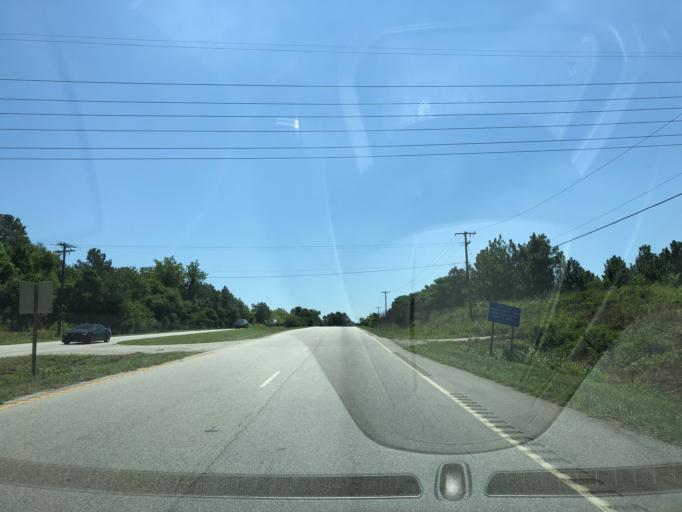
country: US
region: South Carolina
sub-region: Aiken County
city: Clearwater
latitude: 33.4394
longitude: -81.9108
